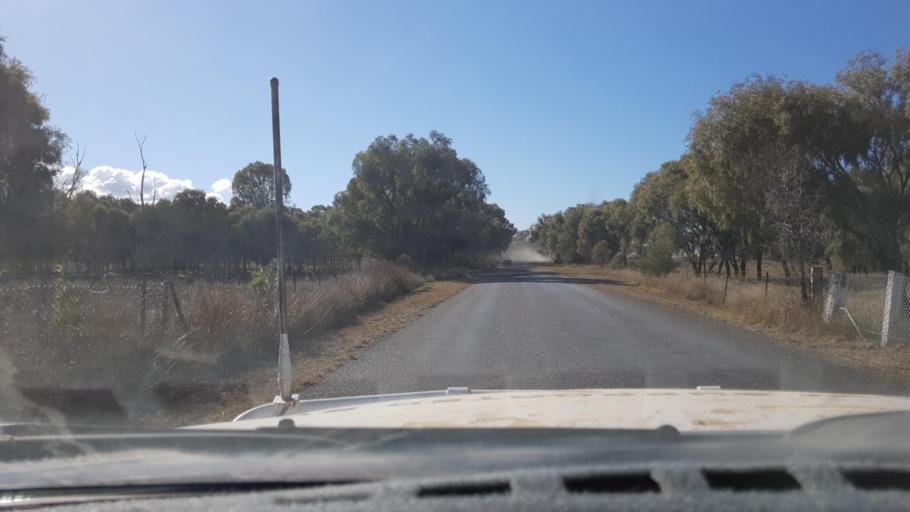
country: AU
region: New South Wales
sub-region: Narrabri
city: Blair Athol
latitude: -30.6754
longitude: 150.4310
